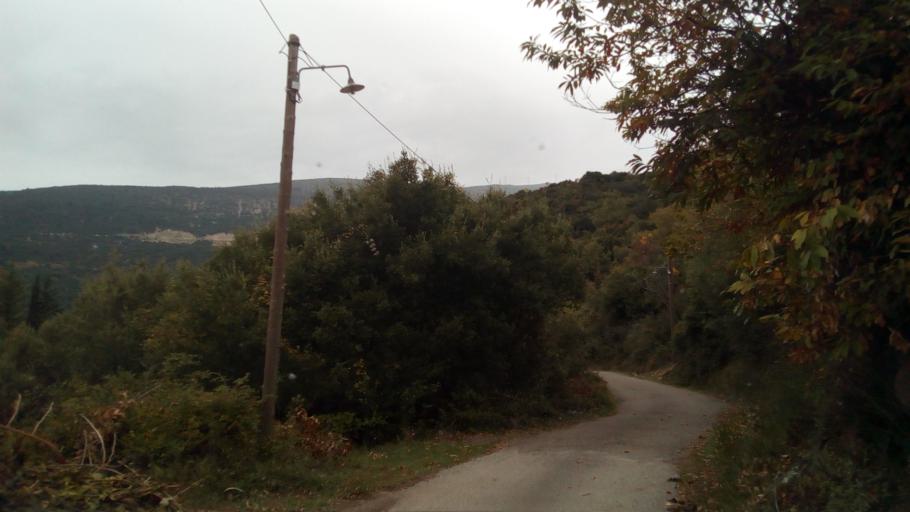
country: GR
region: West Greece
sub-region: Nomos Aitolias kai Akarnanias
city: Thermo
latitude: 38.6042
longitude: 21.8482
